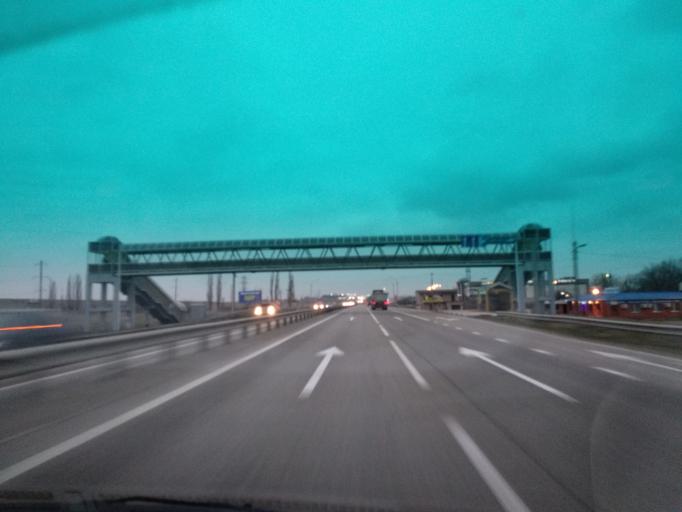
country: RU
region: Adygeya
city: Adygeysk
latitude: 44.9135
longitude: 39.1509
